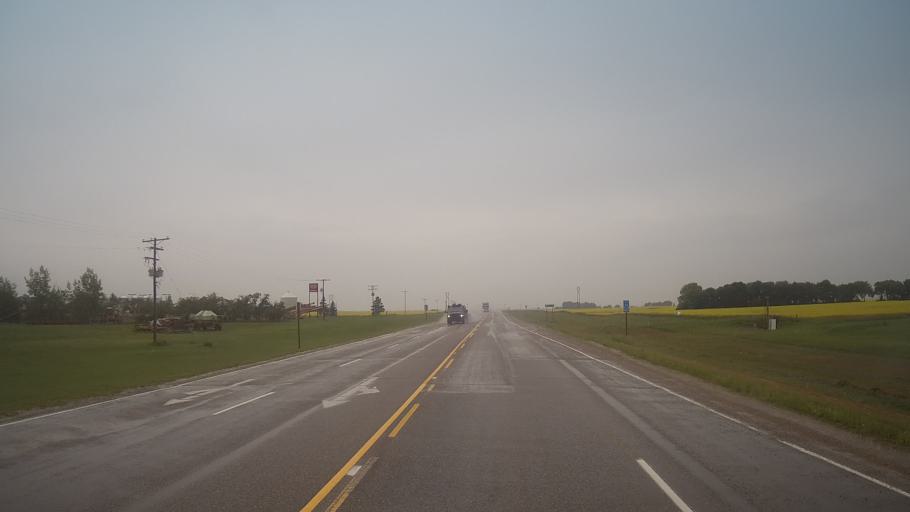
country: CA
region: Saskatchewan
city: Wilkie
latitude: 52.2020
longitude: -108.4559
